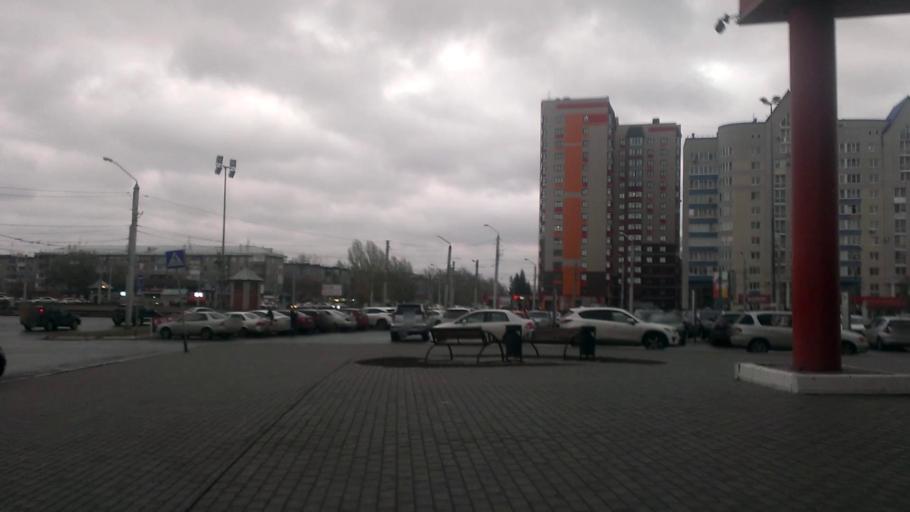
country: RU
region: Altai Krai
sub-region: Gorod Barnaulskiy
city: Barnaul
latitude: 53.3595
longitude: 83.6985
